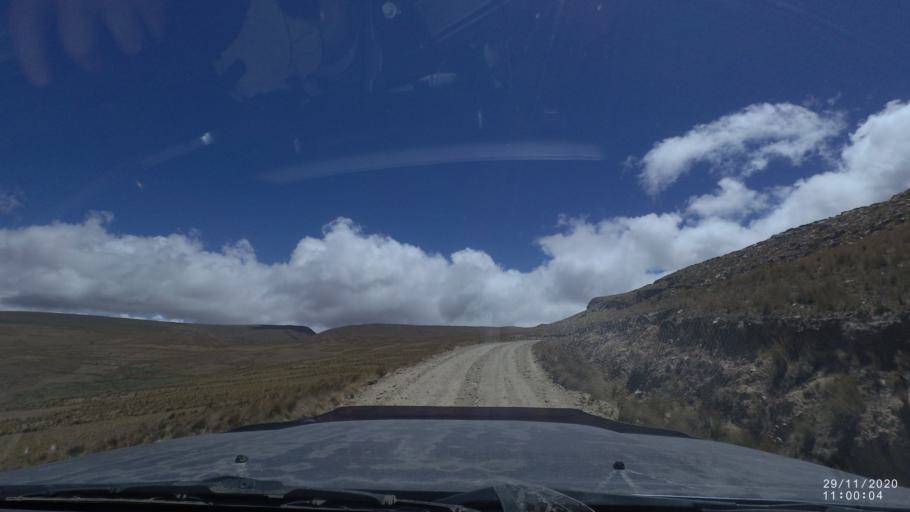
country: BO
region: Cochabamba
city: Cochabamba
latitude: -17.2054
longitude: -66.2281
